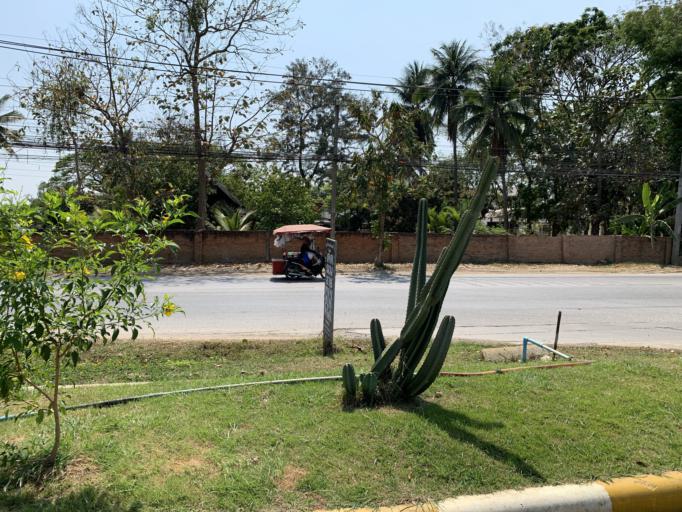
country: TH
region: Lamphun
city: Lamphun
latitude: 18.5882
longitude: 98.9852
